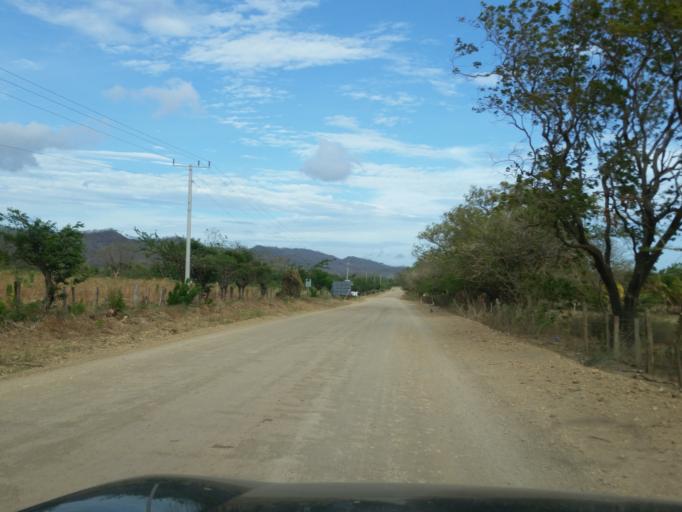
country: NI
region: Rivas
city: Tola
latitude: 11.4329
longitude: -86.0217
